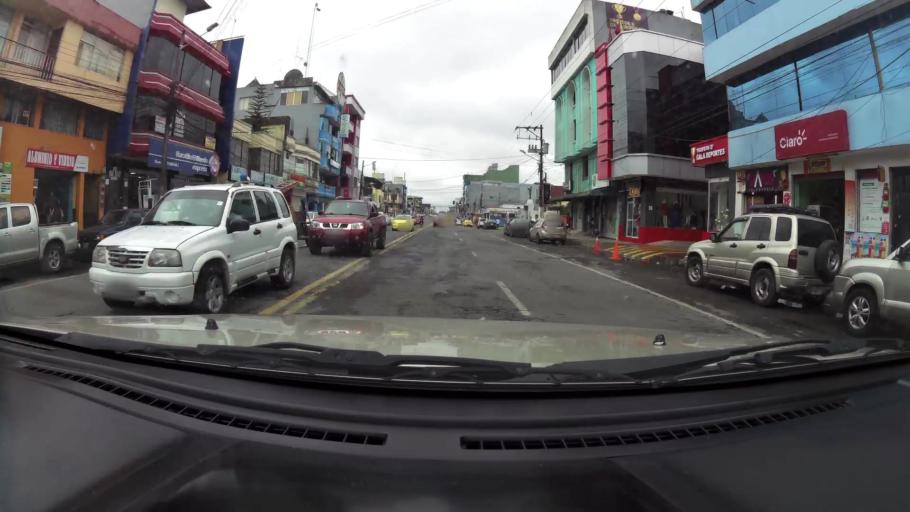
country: EC
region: Santo Domingo de los Tsachilas
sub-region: Canton Santo Domingo de los Colorados
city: Santo Domingo de los Colorados
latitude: -0.2499
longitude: -79.1683
